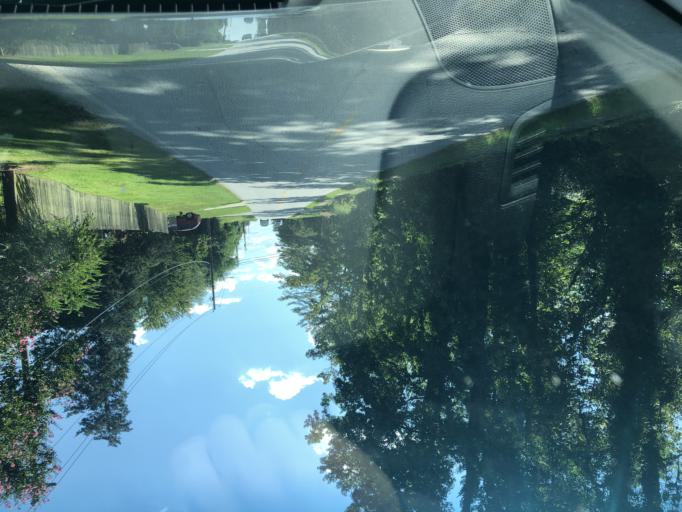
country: US
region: Georgia
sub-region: Muscogee County
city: Columbus
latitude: 32.5397
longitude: -84.9269
